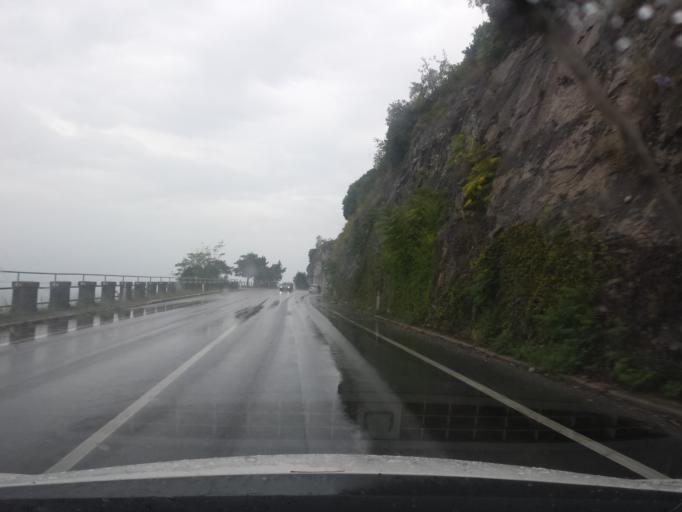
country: IT
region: Friuli Venezia Giulia
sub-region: Provincia di Trieste
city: Aurisina
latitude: 45.7432
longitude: 13.6675
